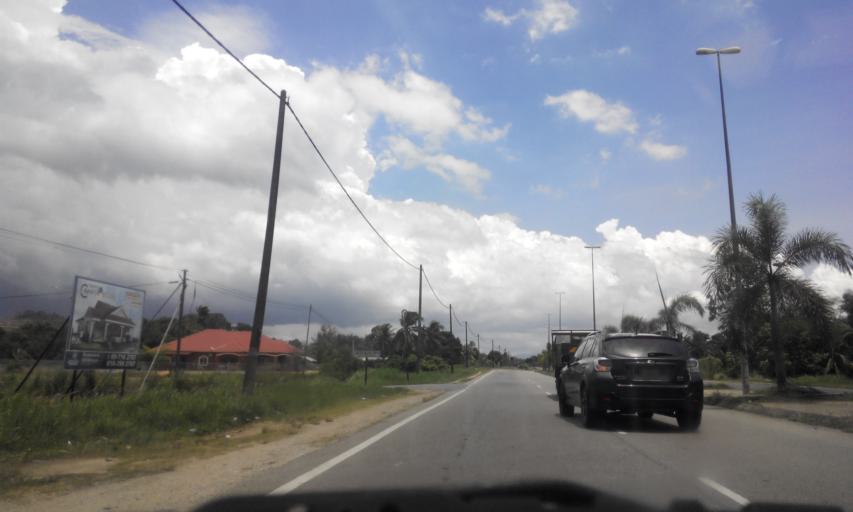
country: MY
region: Perak
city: Parit Buntar
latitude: 5.1224
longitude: 100.5183
